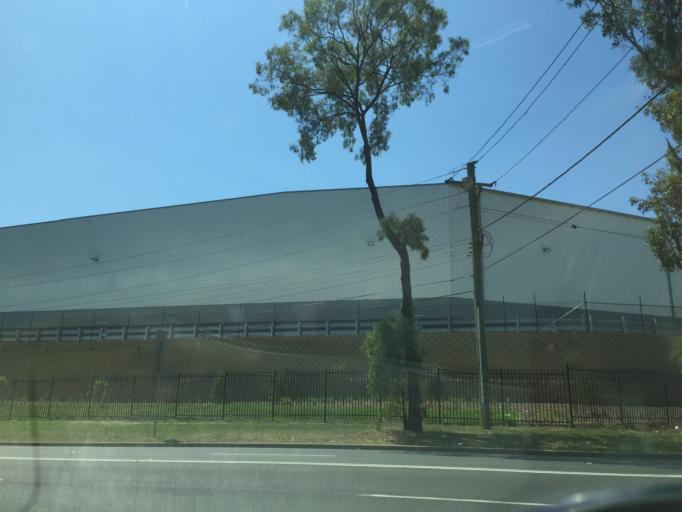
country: AU
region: New South Wales
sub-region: Blacktown
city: Blacktown
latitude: -33.8005
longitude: 150.8963
